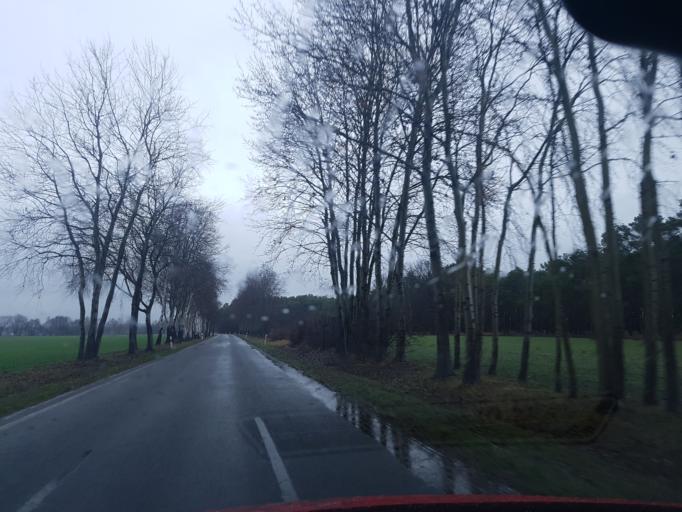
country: DE
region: Brandenburg
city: Schilda
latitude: 51.6181
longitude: 13.3190
